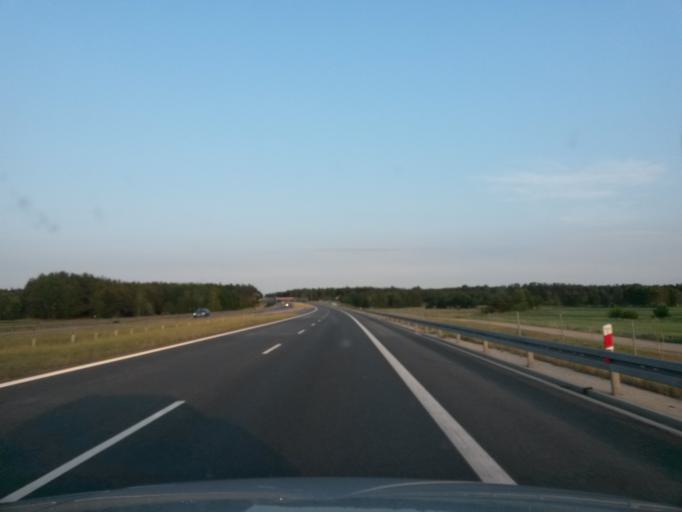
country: PL
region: Lodz Voivodeship
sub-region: Powiat wieruszowski
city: Wieruszow
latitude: 51.3151
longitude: 18.1691
